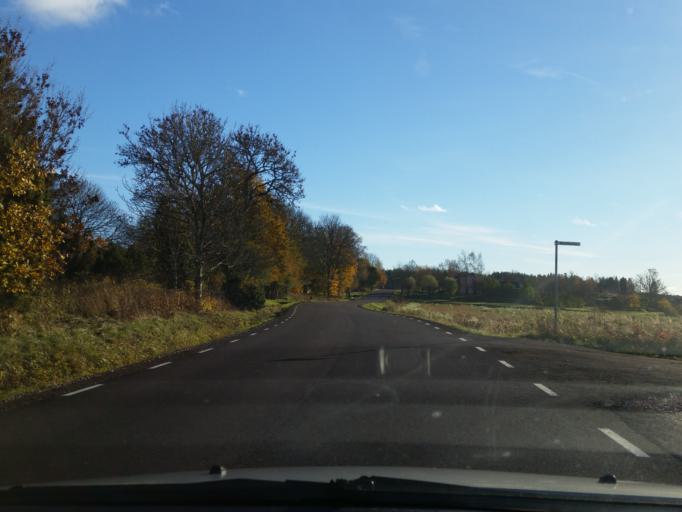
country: AX
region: Alands landsbygd
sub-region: Jomala
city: Jomala
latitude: 60.1881
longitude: 19.9610
